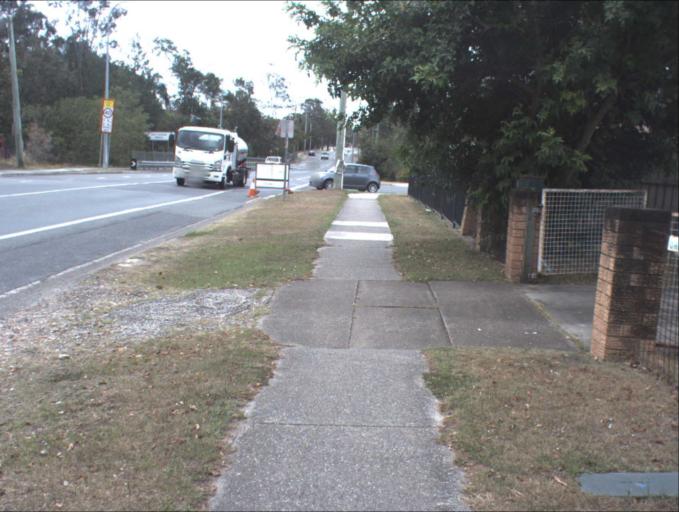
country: AU
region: Queensland
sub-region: Logan
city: Beenleigh
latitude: -27.7126
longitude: 153.1945
